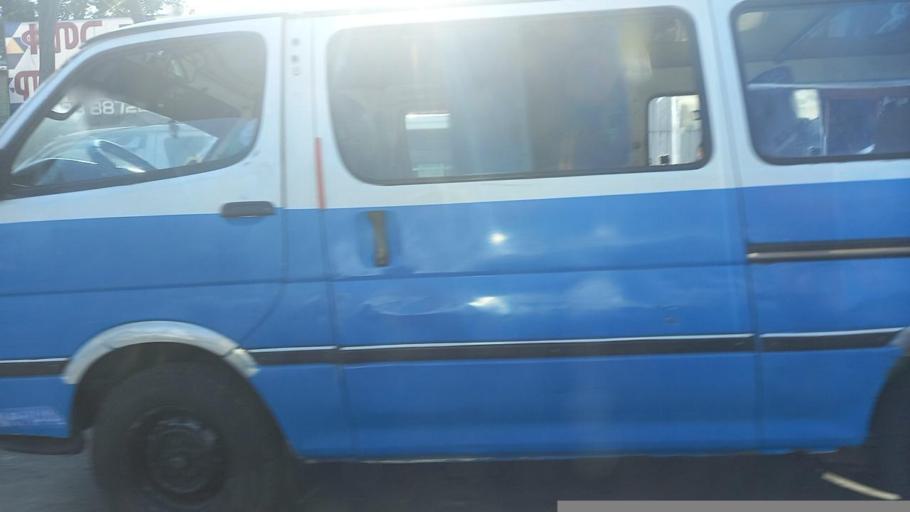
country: ET
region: Adis Abeba
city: Addis Ababa
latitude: 8.9350
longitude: 38.7445
